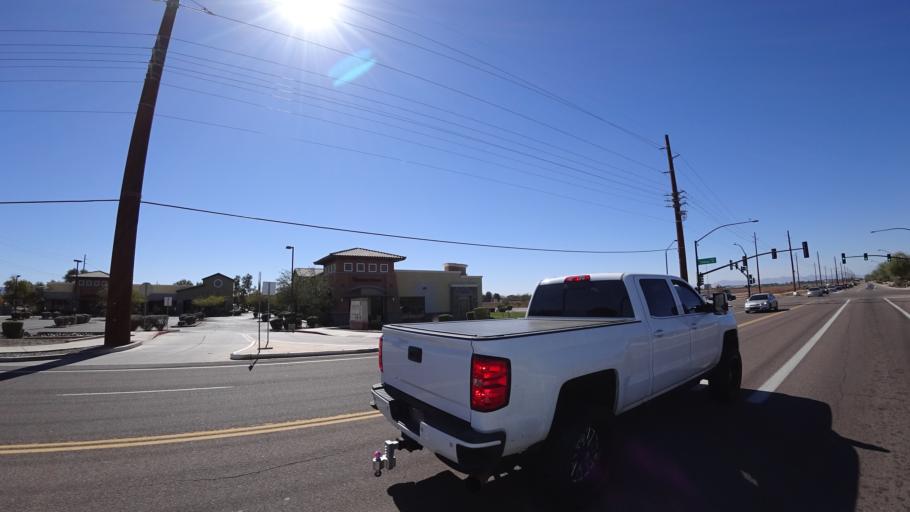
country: US
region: Arizona
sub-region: Maricopa County
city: Gilbert
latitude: 33.2921
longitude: -111.7735
